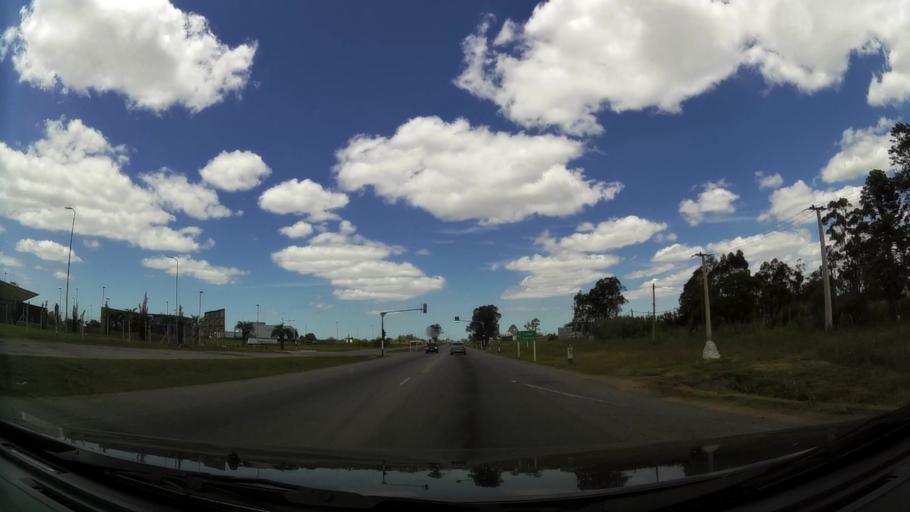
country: UY
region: Canelones
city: Colonia Nicolich
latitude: -34.8121
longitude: -56.0068
